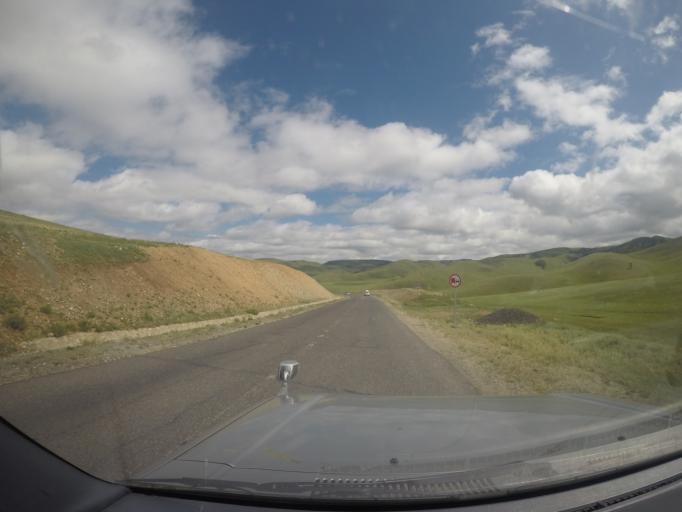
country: MN
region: Hentiy
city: Modot
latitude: 47.7944
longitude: 108.7631
